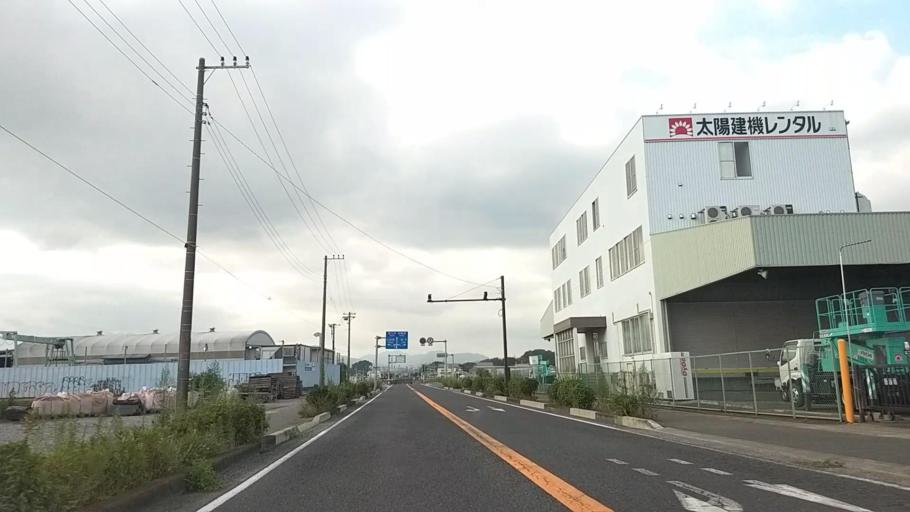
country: JP
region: Kanagawa
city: Isehara
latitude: 35.3711
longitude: 139.3212
